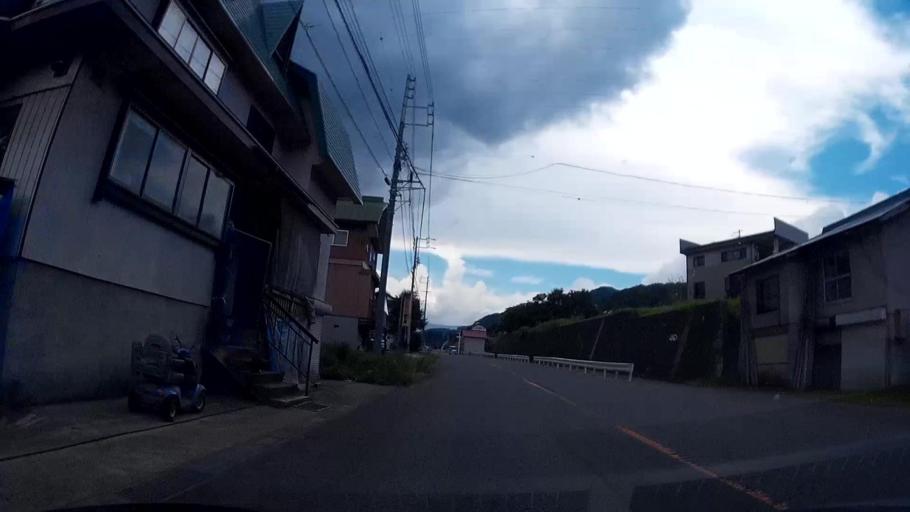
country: JP
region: Nagano
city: Iiyama
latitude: 36.9852
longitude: 138.5345
